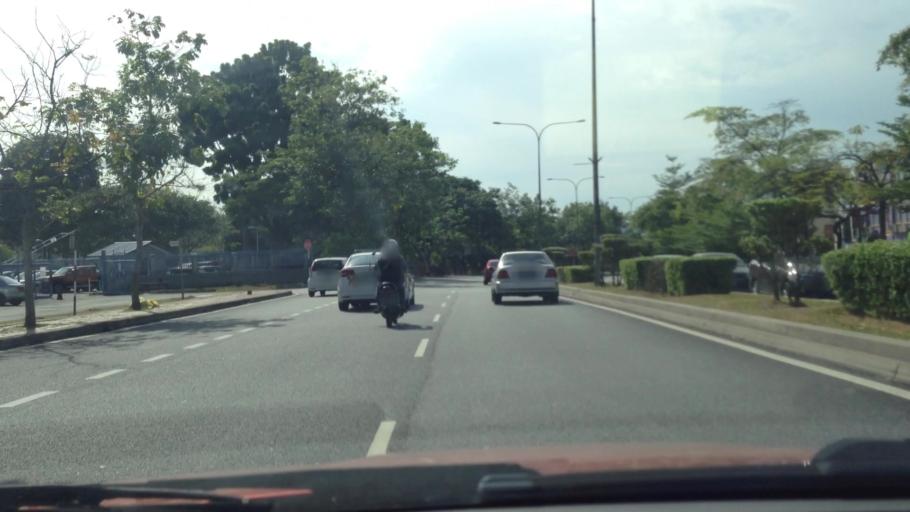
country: MY
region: Selangor
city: Subang Jaya
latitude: 3.0506
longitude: 101.5834
